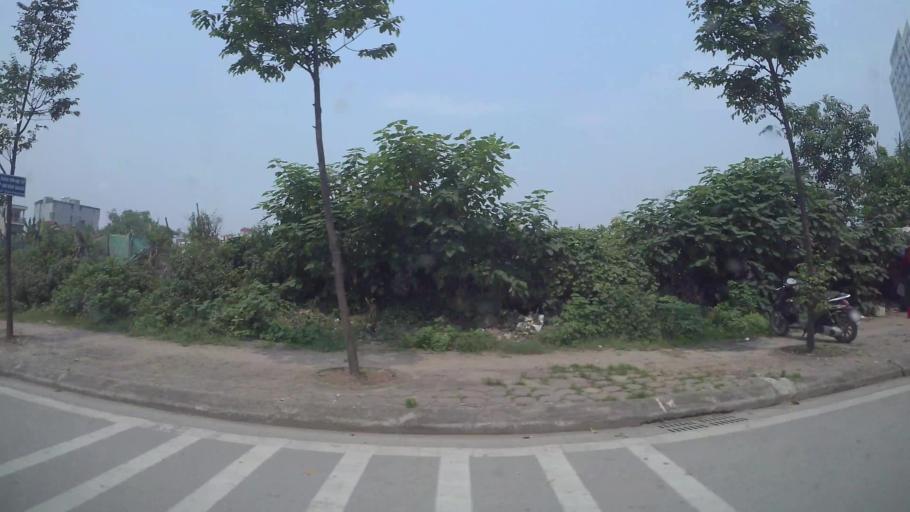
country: VN
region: Ha Noi
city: Van Dien
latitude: 20.9614
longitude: 105.8228
